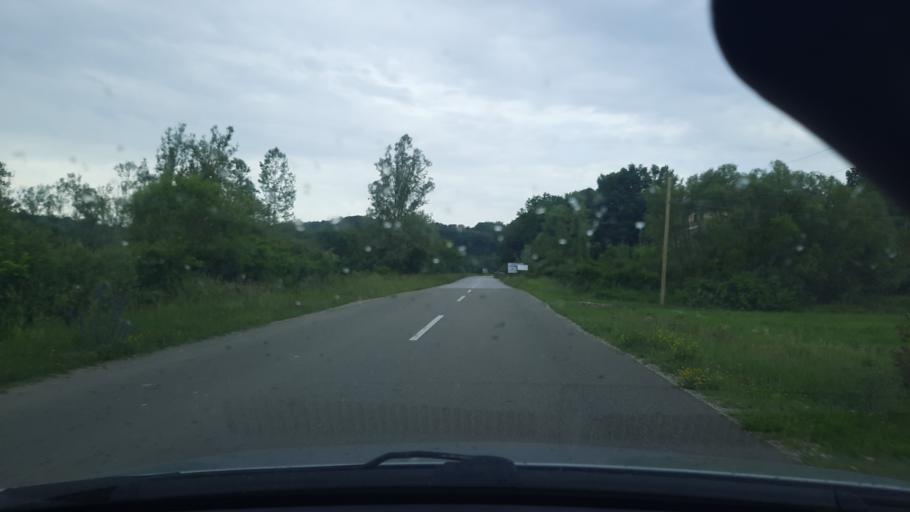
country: RS
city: Jarebice
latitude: 44.4859
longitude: 19.4837
